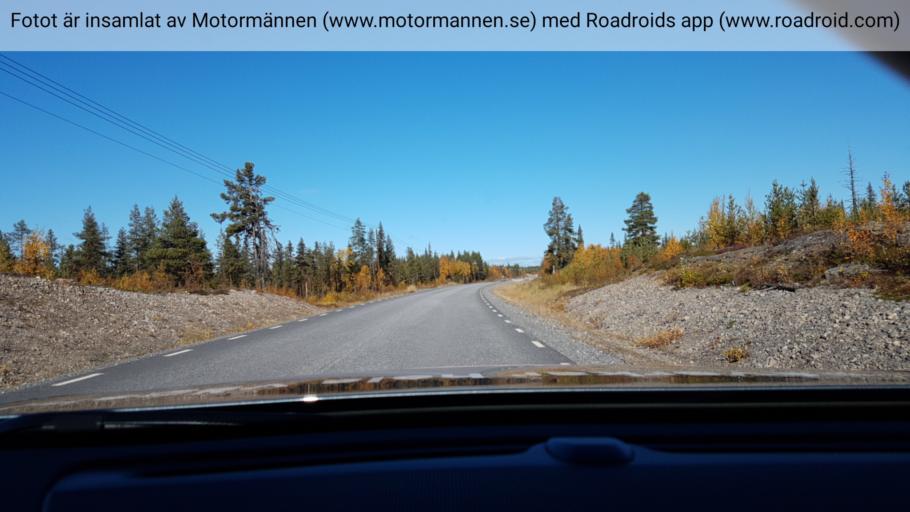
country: SE
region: Norrbotten
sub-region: Gallivare Kommun
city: Gaellivare
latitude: 66.7901
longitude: 21.0384
